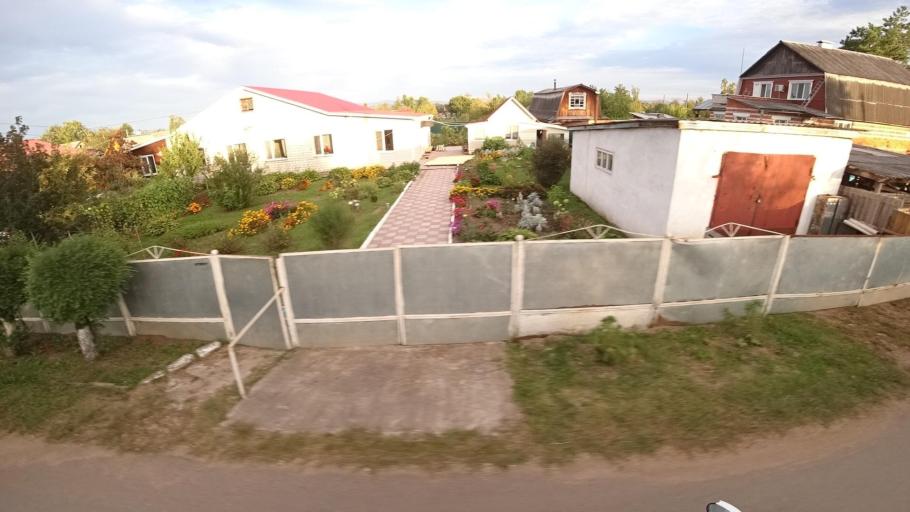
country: RU
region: Primorskiy
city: Yakovlevka
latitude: 44.4268
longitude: 133.4822
